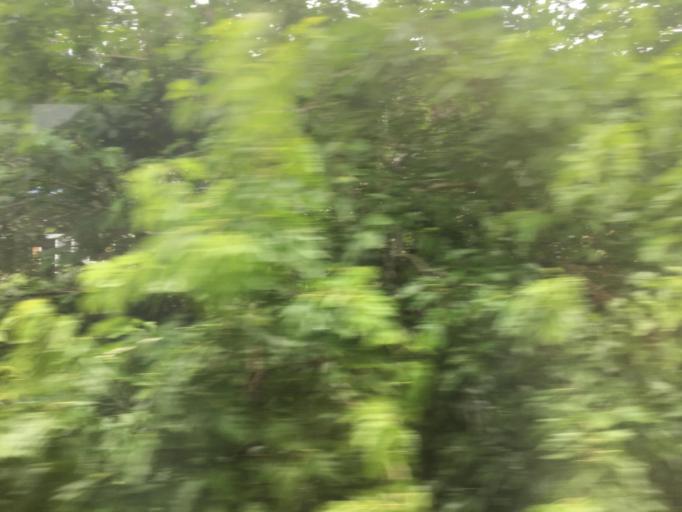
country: JP
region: Gunma
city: Tomioka
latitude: 36.2113
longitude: 138.7938
